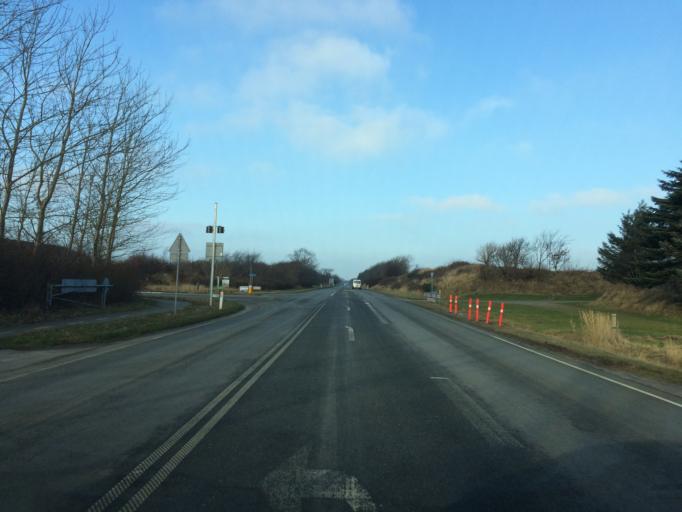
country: DK
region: South Denmark
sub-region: Varde Kommune
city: Oksbol
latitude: 55.5956
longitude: 8.3251
